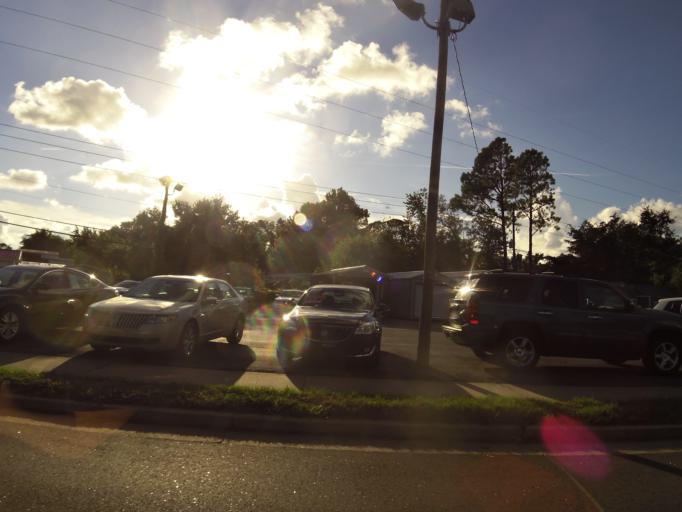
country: US
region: Georgia
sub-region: Glynn County
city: Brunswick
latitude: 31.1785
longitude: -81.4901
